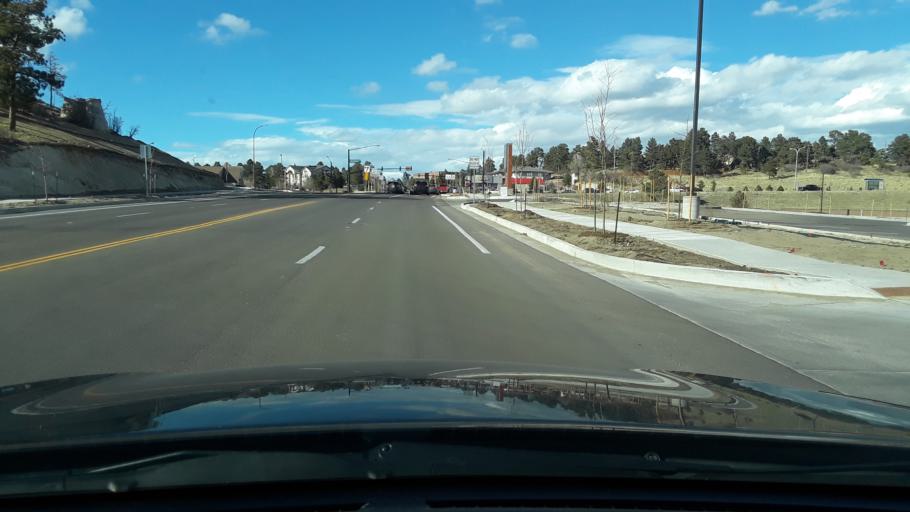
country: US
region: Colorado
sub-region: El Paso County
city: Air Force Academy
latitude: 38.9312
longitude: -104.8079
